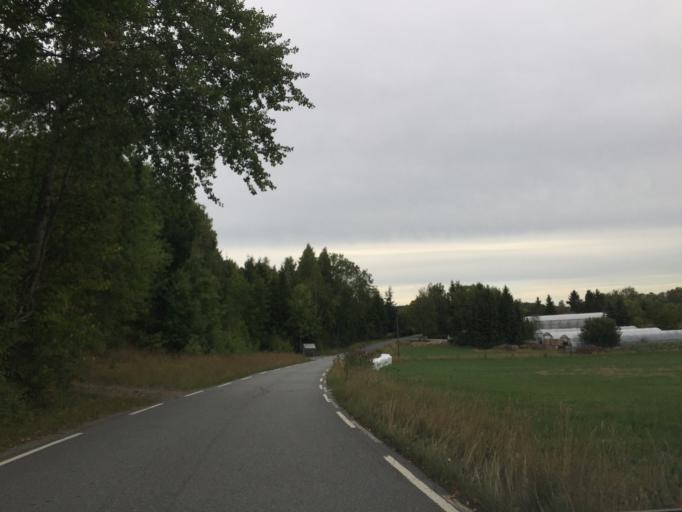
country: NO
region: Ostfold
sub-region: Hvaler
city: Skjaerhalden
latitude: 59.0604
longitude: 11.0339
